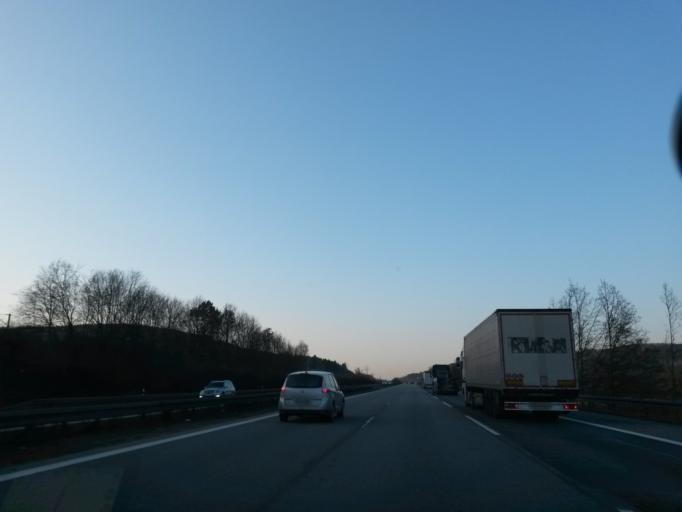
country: DE
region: Bavaria
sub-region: Regierungsbezirk Mittelfranken
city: Thalmassing
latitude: 49.0864
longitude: 11.2882
